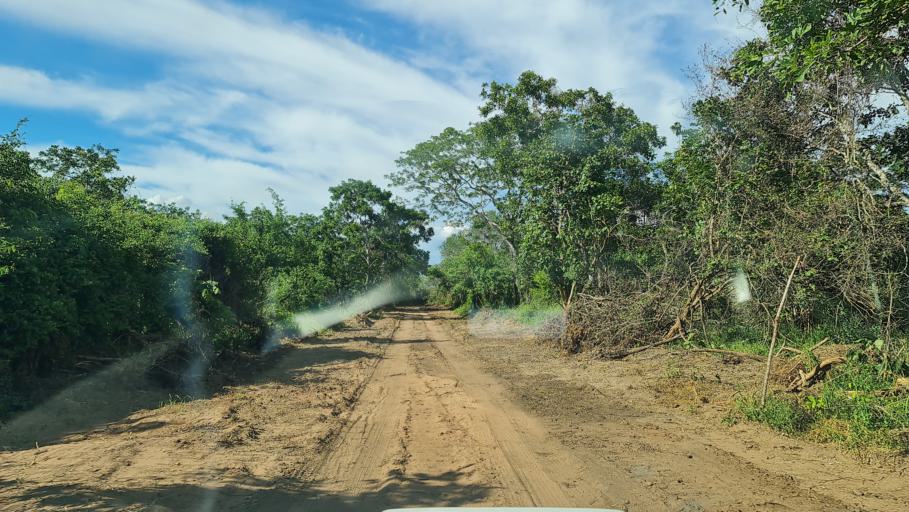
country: MZ
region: Nampula
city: Antonio Enes
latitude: -15.5185
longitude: 40.1293
